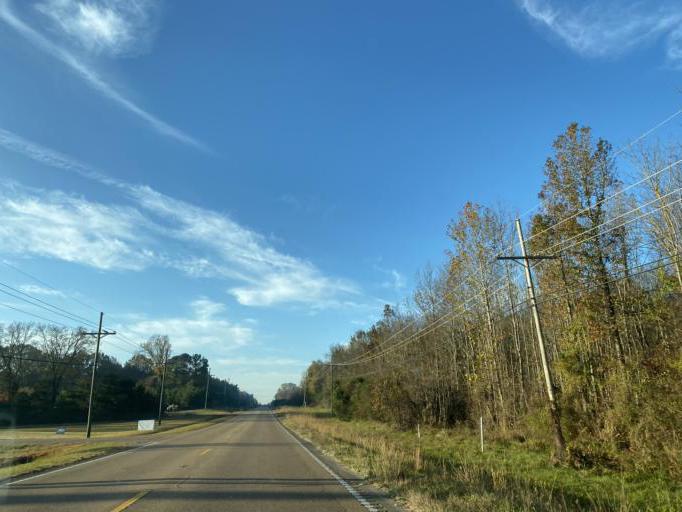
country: US
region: Mississippi
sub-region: Madison County
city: Madison
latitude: 32.5000
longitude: -90.0916
